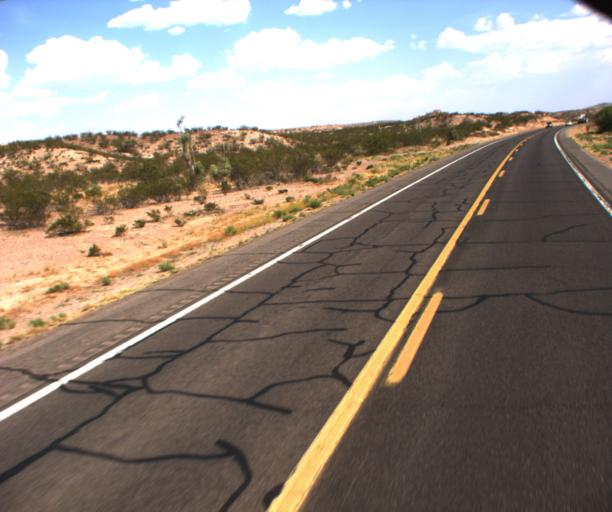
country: US
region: Arizona
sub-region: Greenlee County
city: Clifton
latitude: 32.7929
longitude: -109.1604
